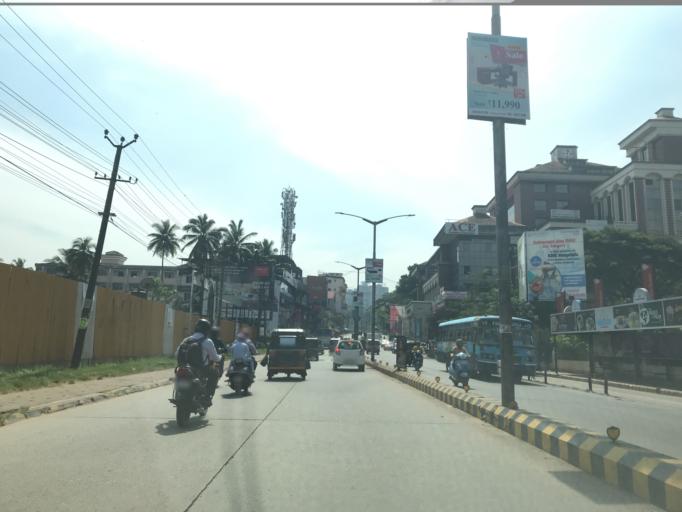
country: IN
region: Karnataka
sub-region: Dakshina Kannada
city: Mangalore
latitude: 12.8809
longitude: 74.8402
